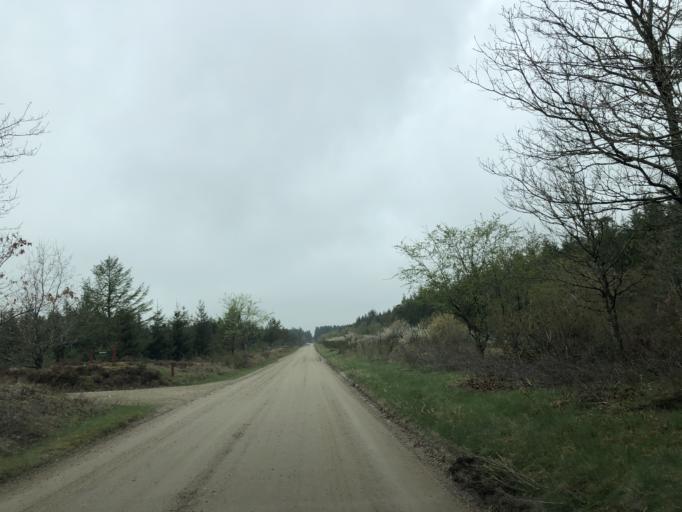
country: DK
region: Central Jutland
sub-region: Lemvig Kommune
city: Lemvig
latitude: 56.4928
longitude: 8.3464
